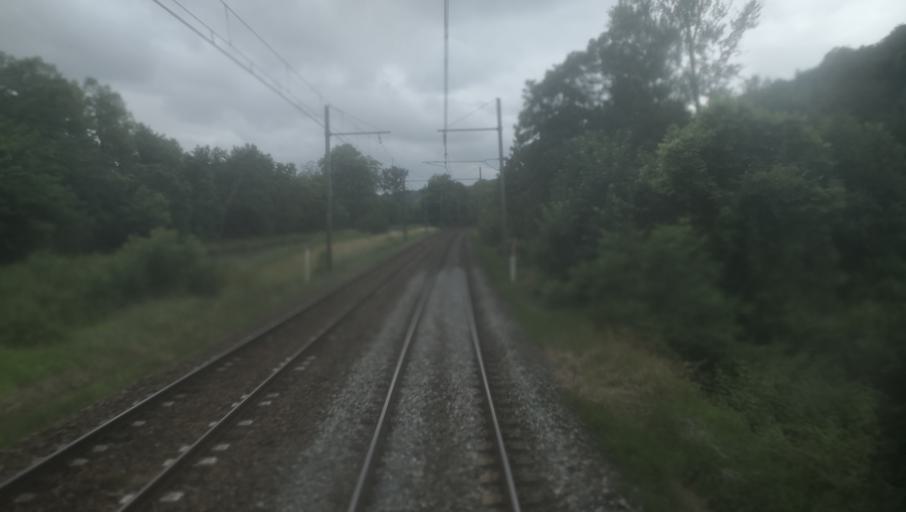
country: FR
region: Midi-Pyrenees
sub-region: Departement du Tarn-et-Garonne
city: Saint-Nicolas-de-la-Grave
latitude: 44.0915
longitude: 1.0133
